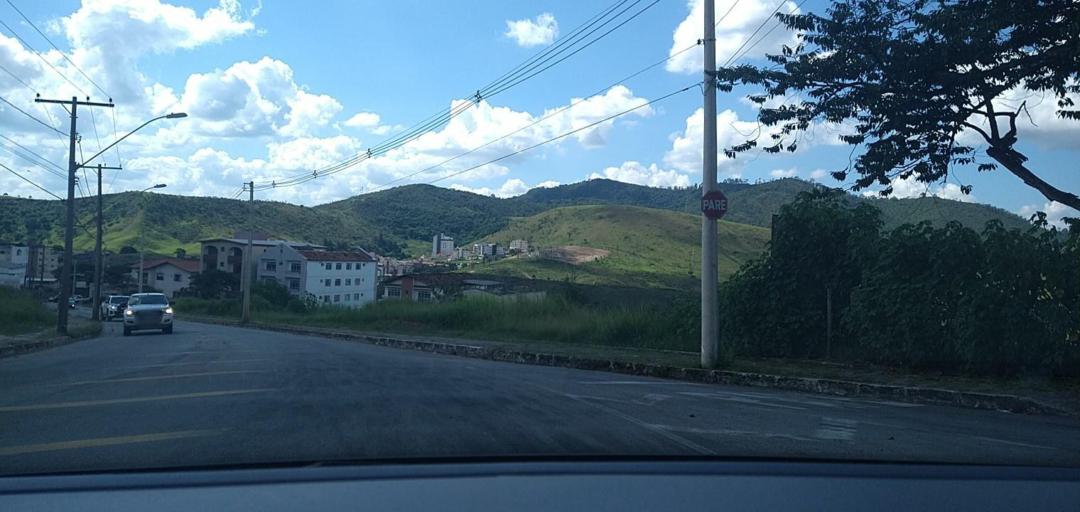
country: BR
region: Minas Gerais
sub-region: Joao Monlevade
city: Joao Monlevade
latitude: -19.8162
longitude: -43.1904
